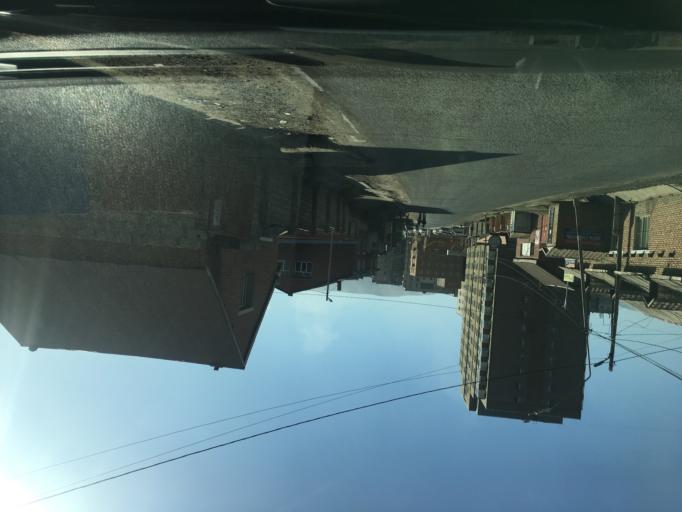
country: MN
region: Ulaanbaatar
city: Ulaanbaatar
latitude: 47.9298
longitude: 106.8768
